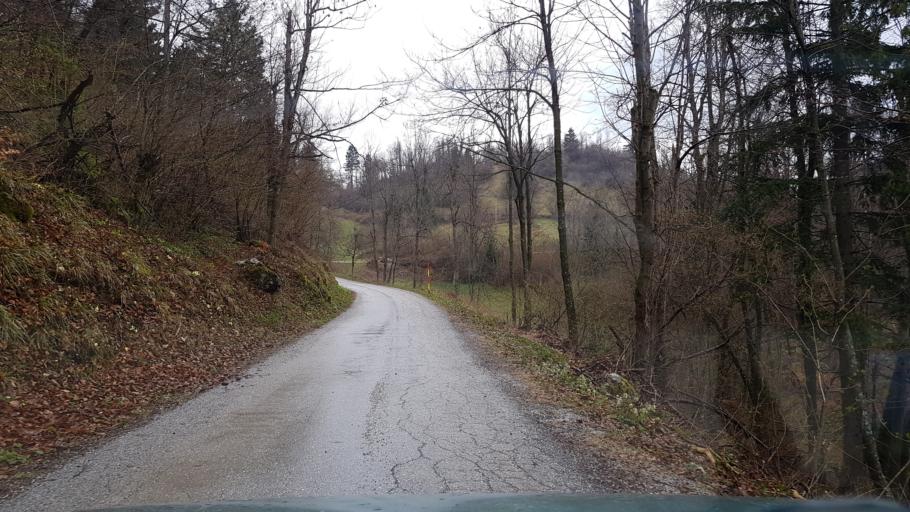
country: SI
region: Cerkno
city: Cerkno
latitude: 46.1410
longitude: 13.8787
